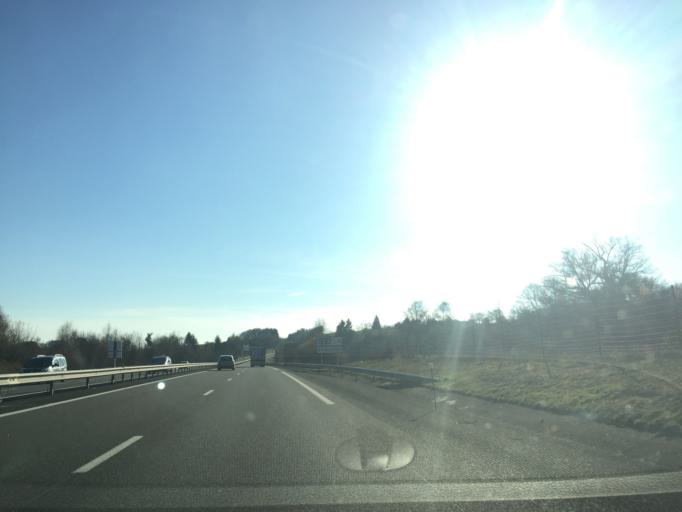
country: FR
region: Limousin
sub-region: Departement de la Correze
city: Sainte-Fereole
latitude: 45.2986
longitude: 1.5734
